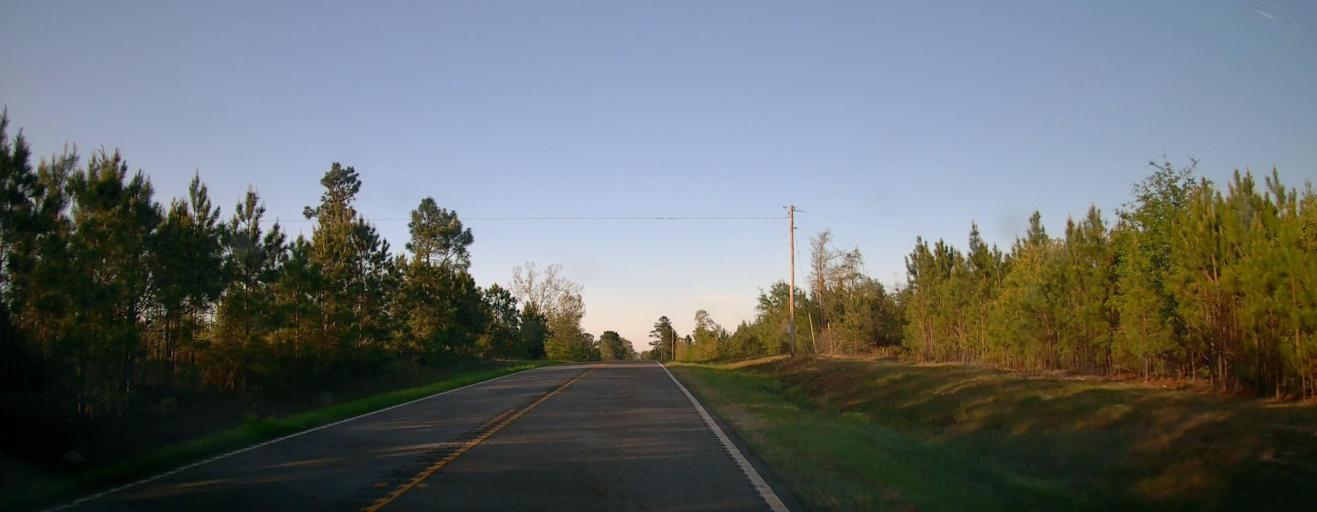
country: US
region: Georgia
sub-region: Marion County
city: Buena Vista
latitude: 32.4249
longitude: -84.4319
